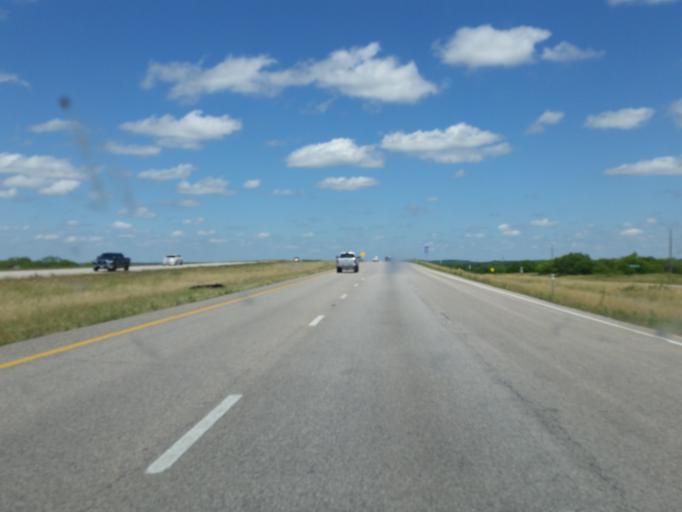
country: US
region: Texas
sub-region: Eastland County
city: Cisco
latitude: 32.3757
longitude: -99.1723
